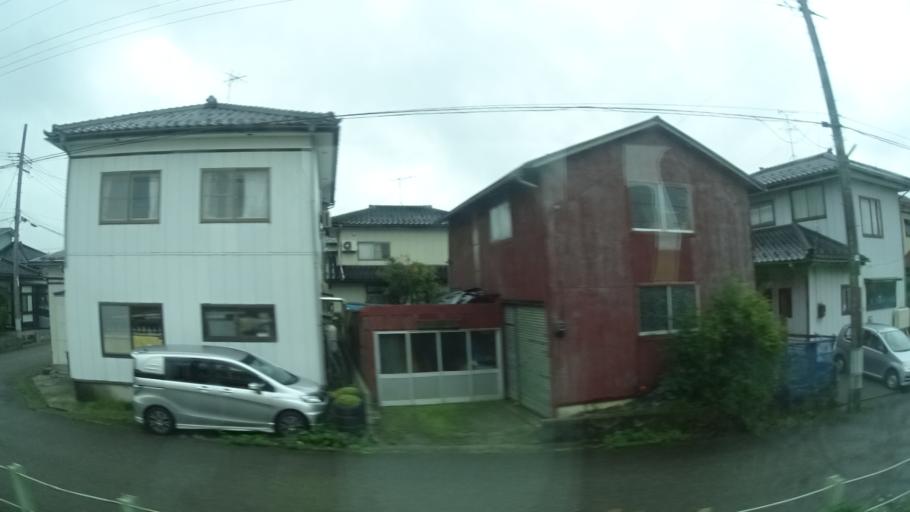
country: JP
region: Yamagata
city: Tsuruoka
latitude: 38.7407
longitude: 139.8212
